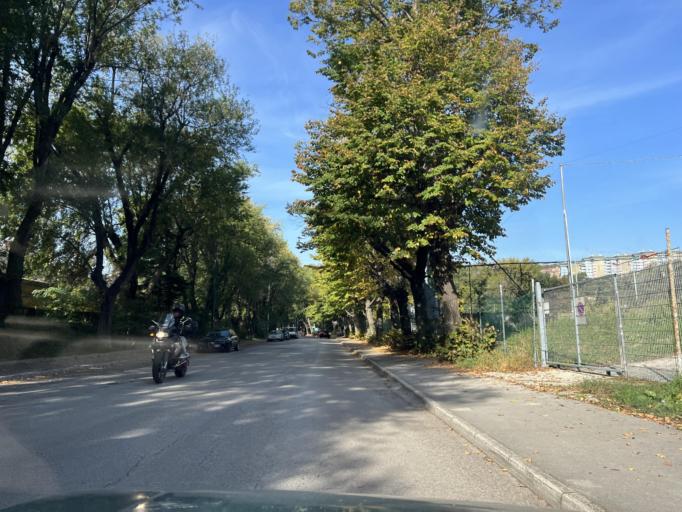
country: IT
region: Friuli Venezia Giulia
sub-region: Provincia di Trieste
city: Domio
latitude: 45.6171
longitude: 13.8222
